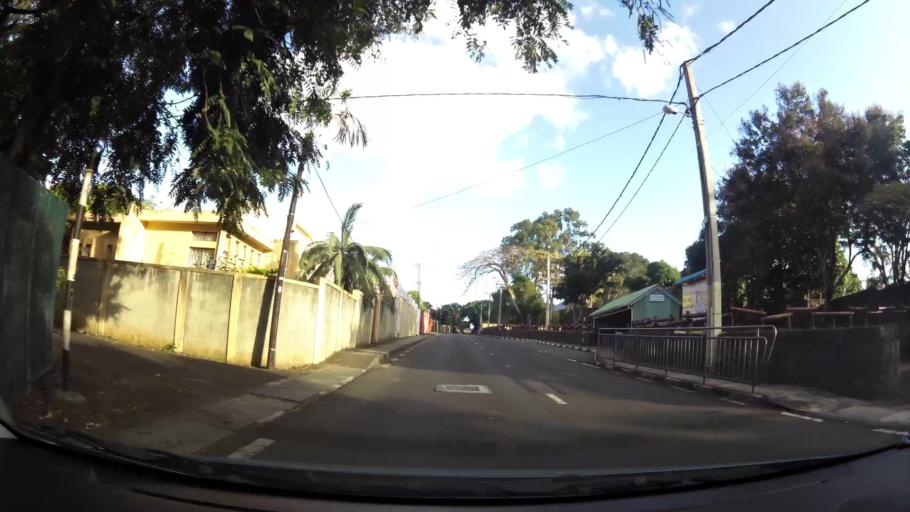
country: MU
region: Moka
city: Moka
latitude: -20.2262
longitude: 57.4636
